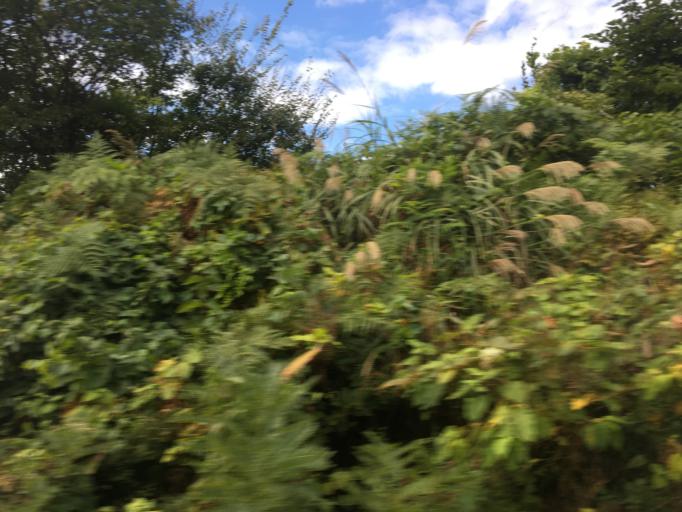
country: JP
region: Aomori
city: Shimokizukuri
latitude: 40.7762
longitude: 140.1880
